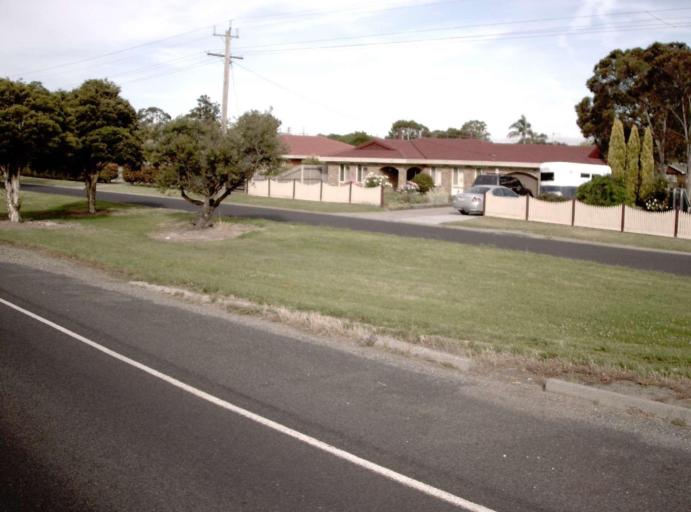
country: AU
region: Victoria
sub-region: Latrobe
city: Traralgon
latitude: -38.1230
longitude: 146.5710
